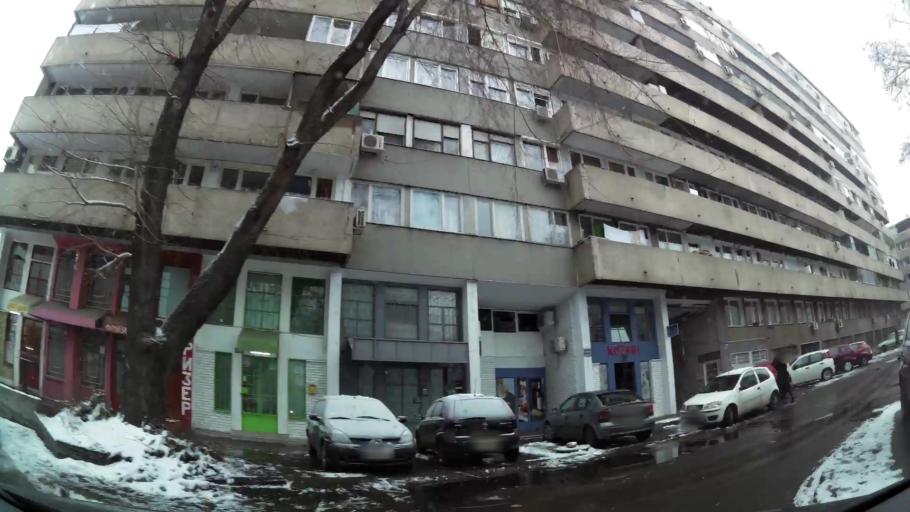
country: RS
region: Central Serbia
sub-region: Belgrade
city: Zemun
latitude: 44.8255
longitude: 20.4028
